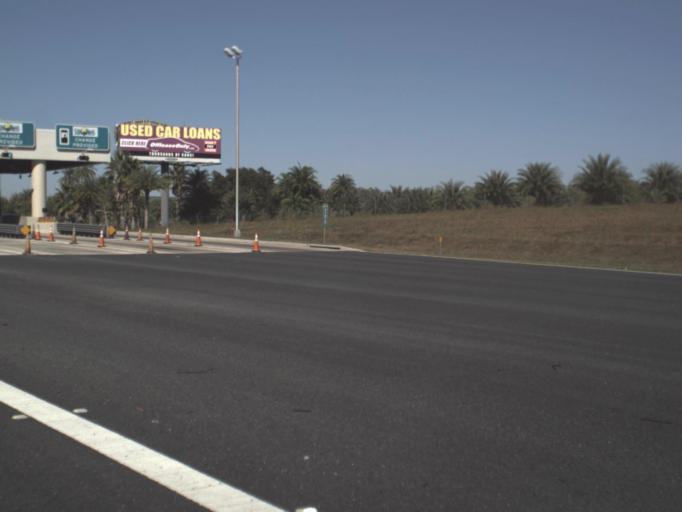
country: US
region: Florida
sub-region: Lake County
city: Yalaha
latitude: 28.6690
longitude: -81.8405
